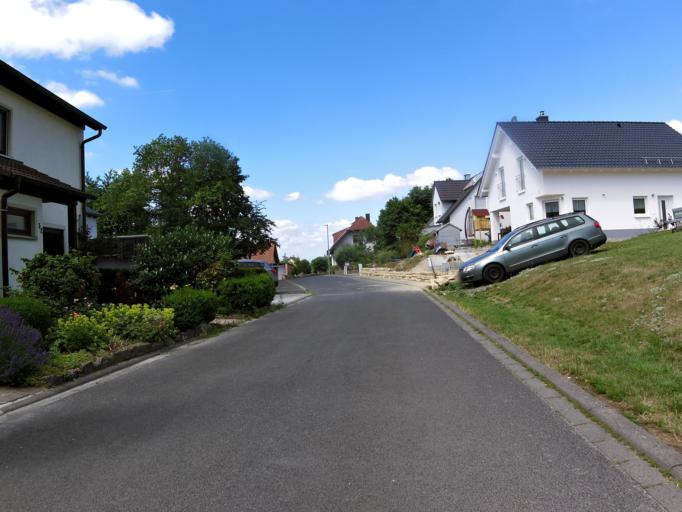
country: DE
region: Bavaria
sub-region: Regierungsbezirk Unterfranken
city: Kist
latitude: 49.7473
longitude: 9.8426
